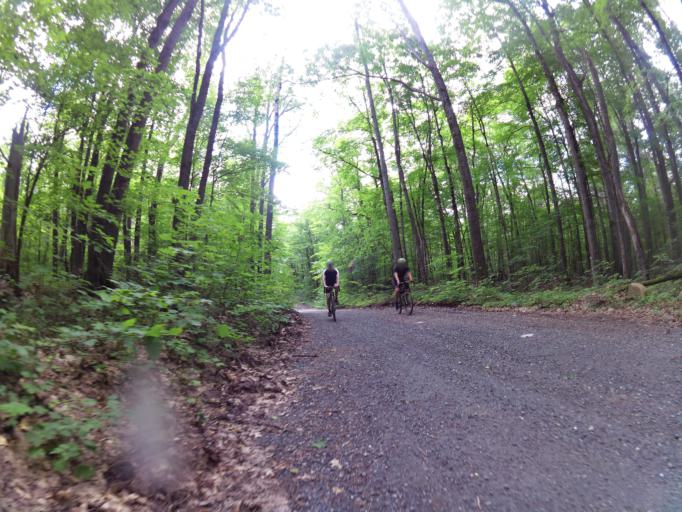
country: CA
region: Ontario
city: Perth
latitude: 45.0285
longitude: -76.5653
